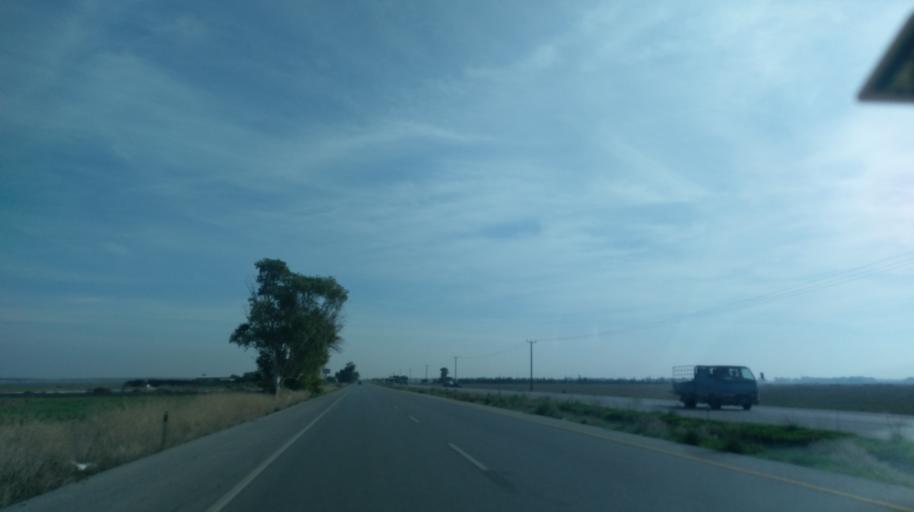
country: CY
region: Larnaka
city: Athienou
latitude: 35.2113
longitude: 33.5467
